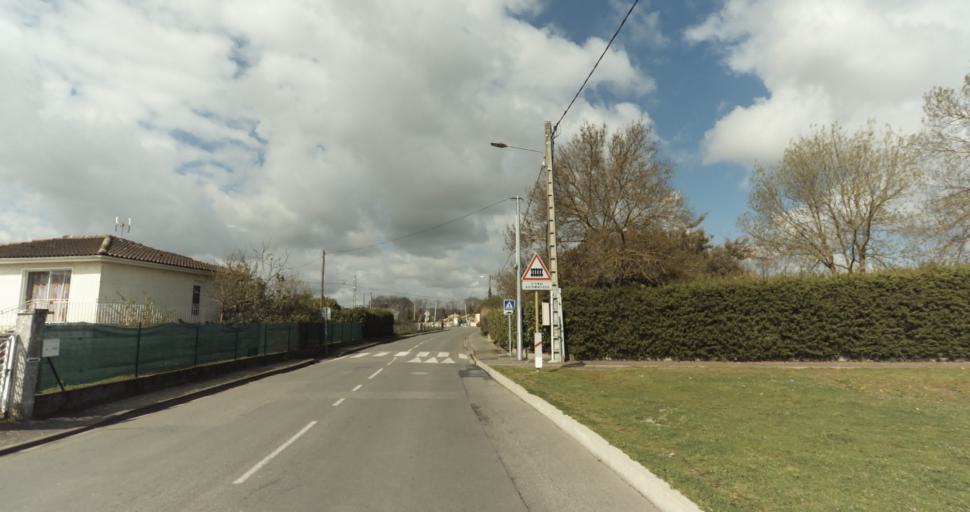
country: FR
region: Midi-Pyrenees
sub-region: Departement de la Haute-Garonne
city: Auterive
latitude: 43.3551
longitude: 1.4644
